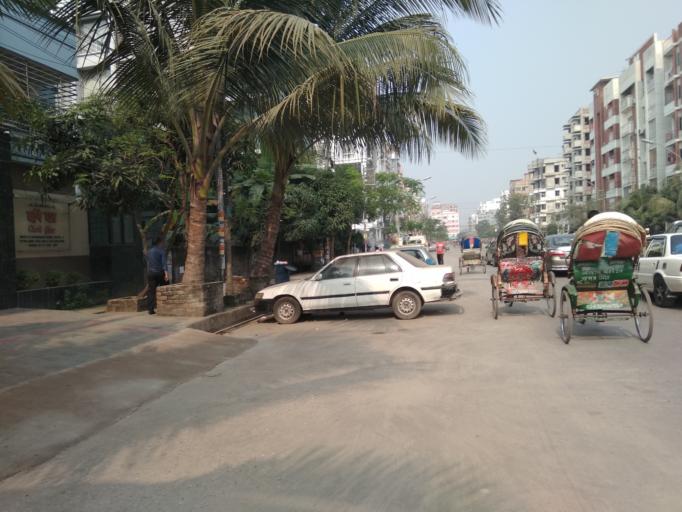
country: BD
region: Dhaka
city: Tungi
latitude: 23.8714
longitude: 90.3839
